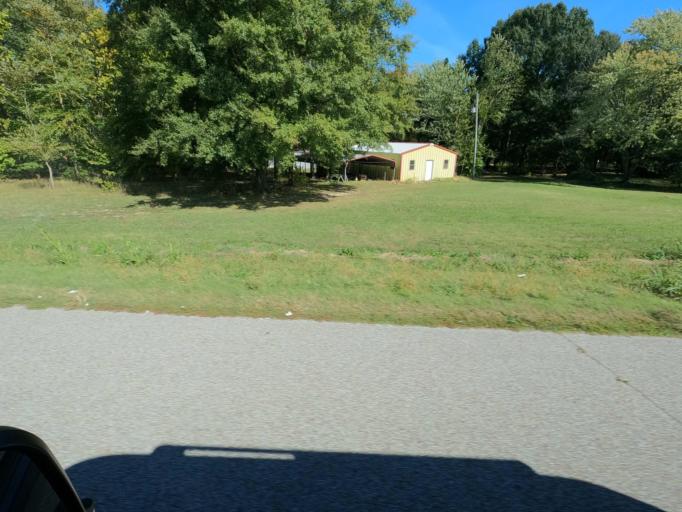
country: US
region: Tennessee
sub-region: Crockett County
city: Alamo
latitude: 35.7491
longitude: -89.1052
